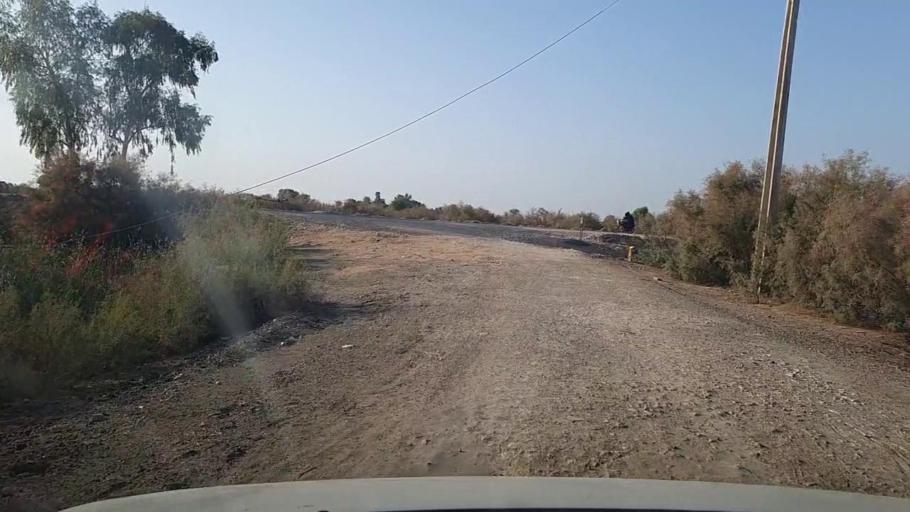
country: PK
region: Sindh
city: Kandhkot
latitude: 28.3113
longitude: 69.3272
